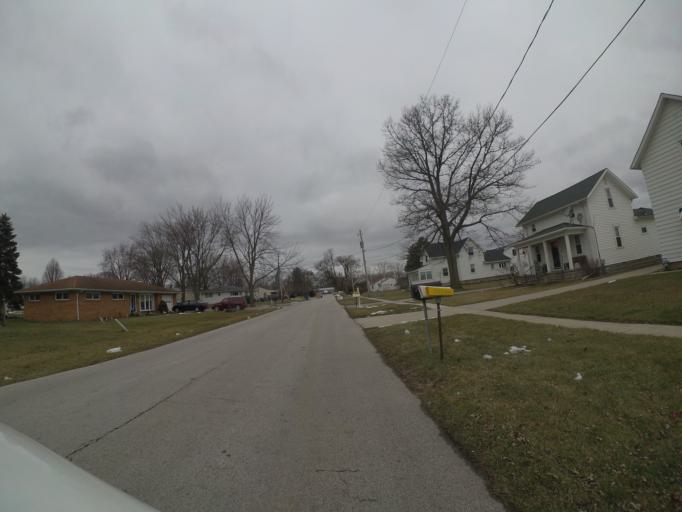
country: US
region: Ohio
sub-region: Wood County
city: Walbridge
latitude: 41.5627
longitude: -83.5097
